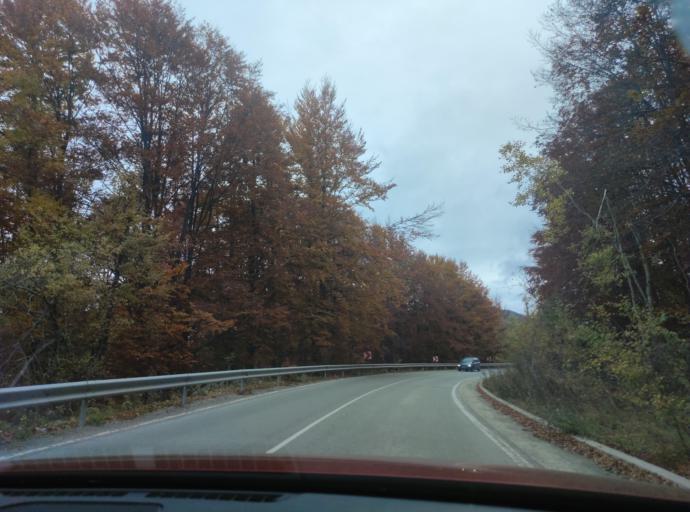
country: BG
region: Sofiya
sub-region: Obshtina Godech
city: Godech
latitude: 43.1079
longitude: 23.1093
